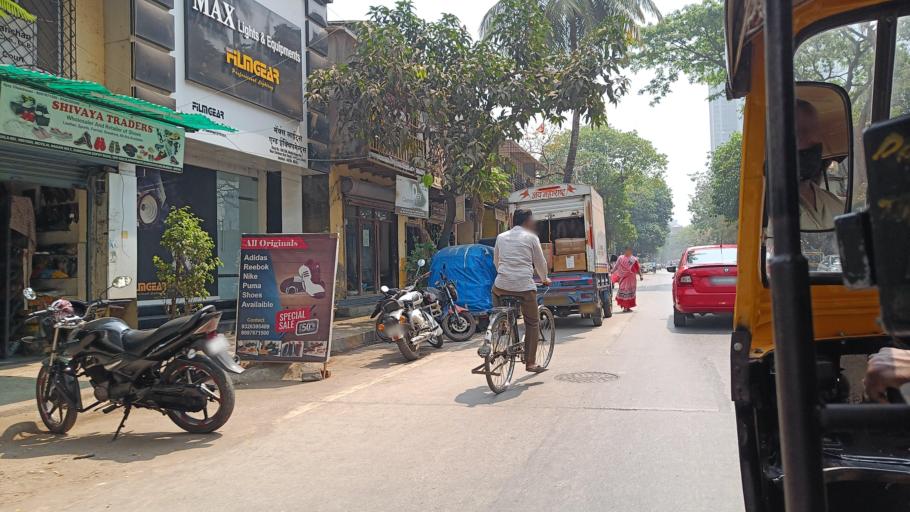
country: IN
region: Maharashtra
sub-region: Mumbai Suburban
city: Powai
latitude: 19.1552
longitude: 72.8368
